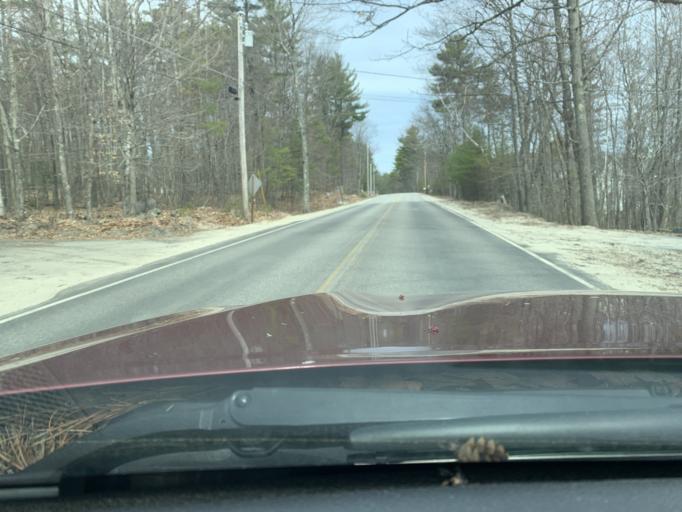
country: US
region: Maine
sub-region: Cumberland County
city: Raymond
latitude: 43.9438
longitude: -70.3850
